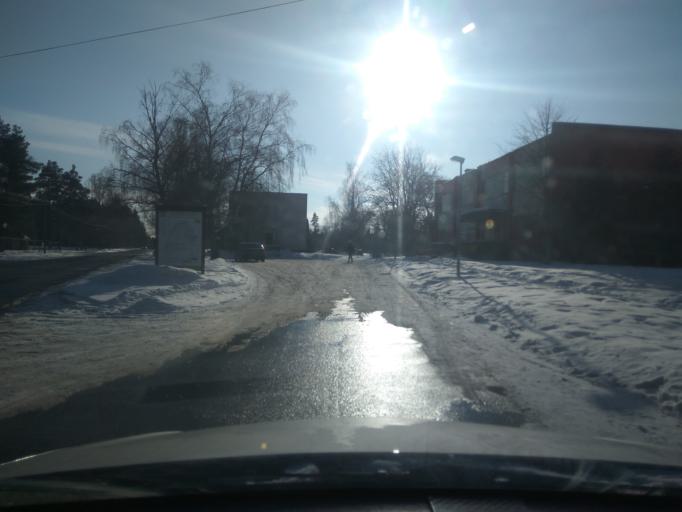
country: LV
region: Kuldigas Rajons
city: Kuldiga
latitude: 57.2769
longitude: 22.0213
